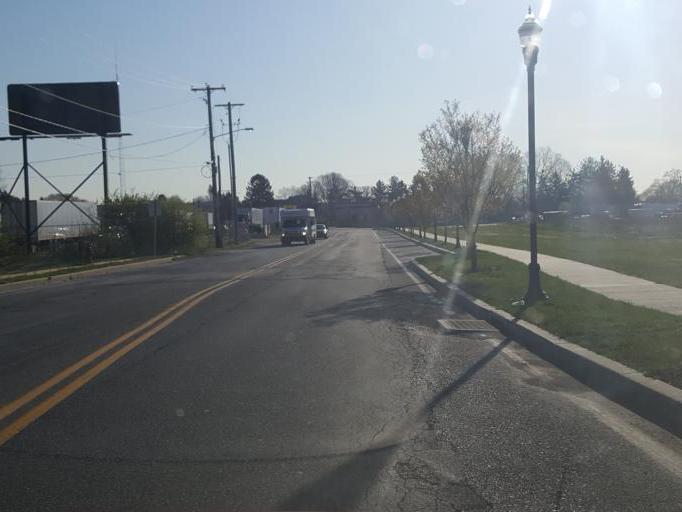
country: US
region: Pennsylvania
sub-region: Lancaster County
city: Lancaster
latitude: 40.0565
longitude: -76.3021
